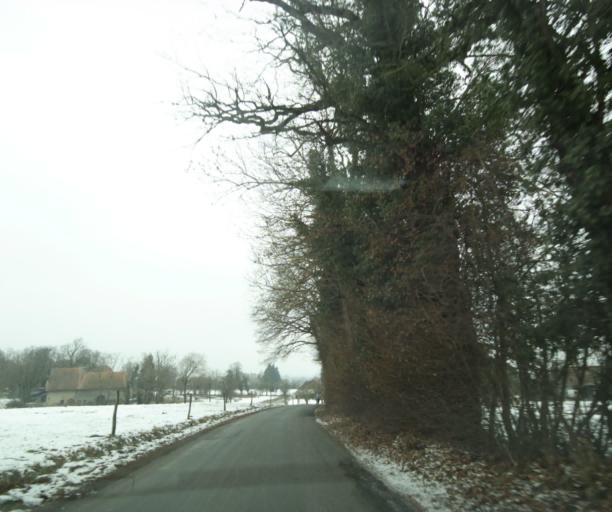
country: FR
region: Rhone-Alpes
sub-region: Departement de la Haute-Savoie
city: Reignier-Esery
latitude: 46.1218
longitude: 6.2779
